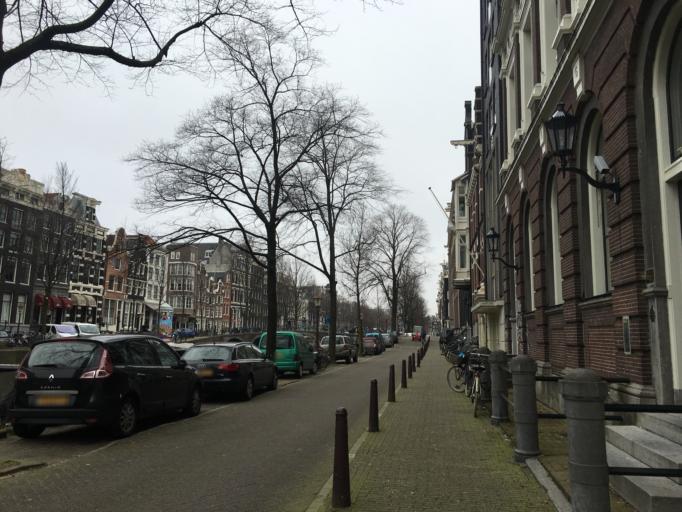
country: NL
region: North Holland
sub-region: Gemeente Amsterdam
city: Amsterdam
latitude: 52.3761
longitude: 4.8892
